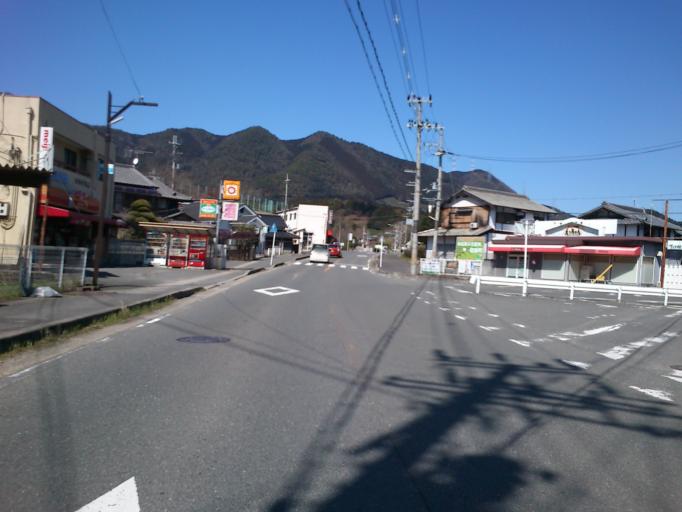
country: JP
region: Kyoto
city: Uji
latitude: 34.8007
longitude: 135.9086
